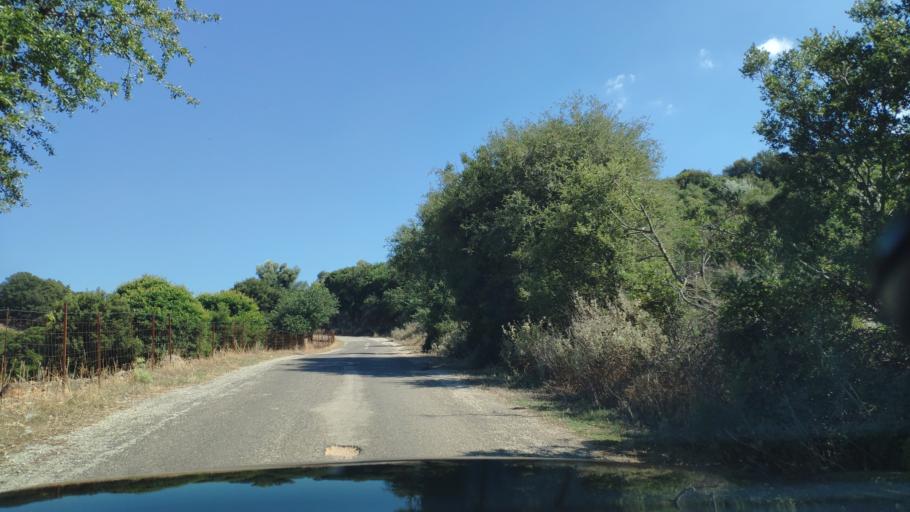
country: GR
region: West Greece
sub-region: Nomos Aitolias kai Akarnanias
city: Katouna
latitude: 38.8111
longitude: 21.1060
